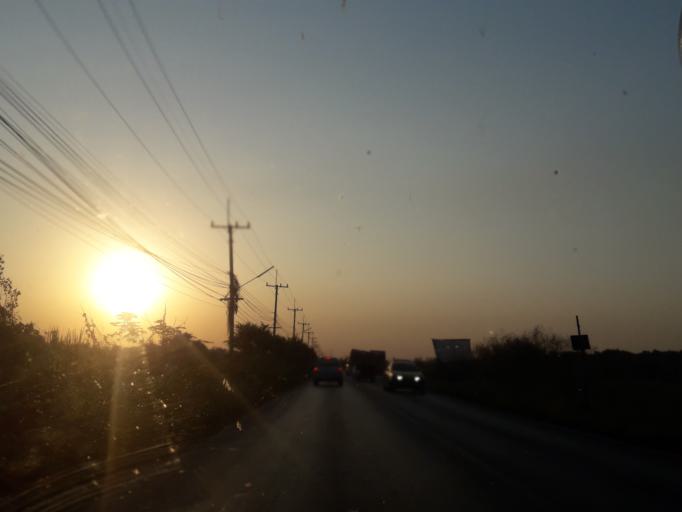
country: TH
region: Pathum Thani
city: Nong Suea
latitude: 14.1316
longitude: 100.8001
